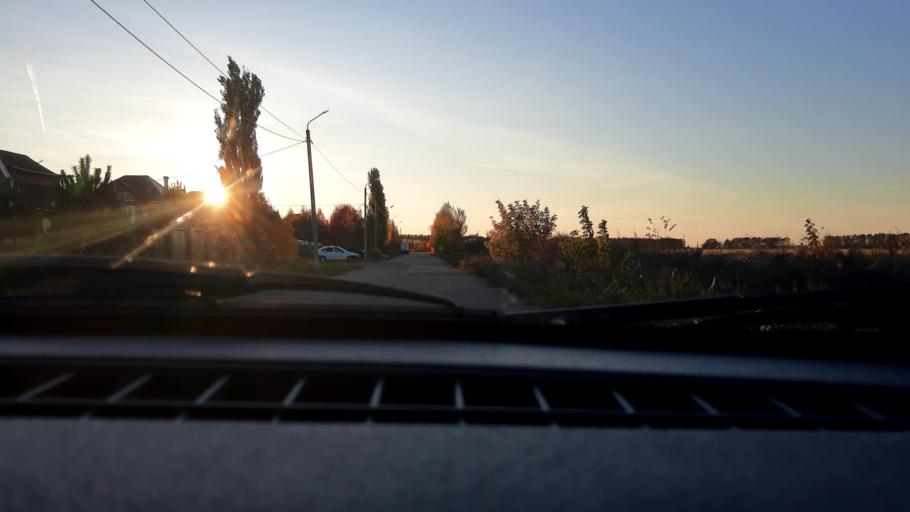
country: RU
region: Bashkortostan
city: Ufa
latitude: 54.8586
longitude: 56.0197
